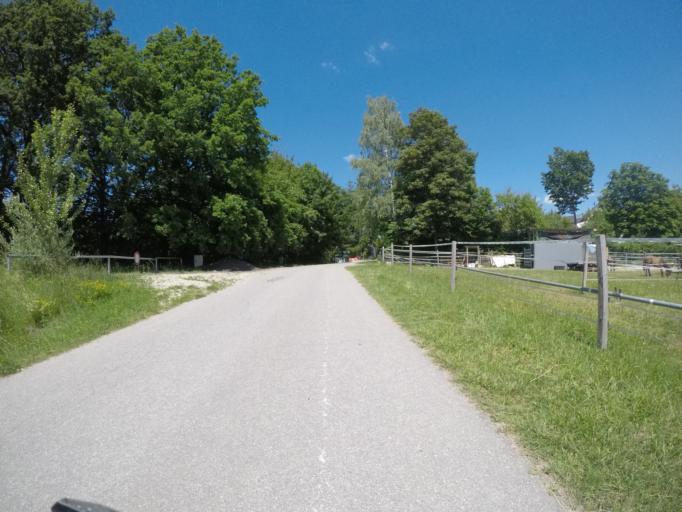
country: DE
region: Bavaria
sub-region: Lower Bavaria
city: Kumhausen
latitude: 48.4860
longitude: 12.1788
